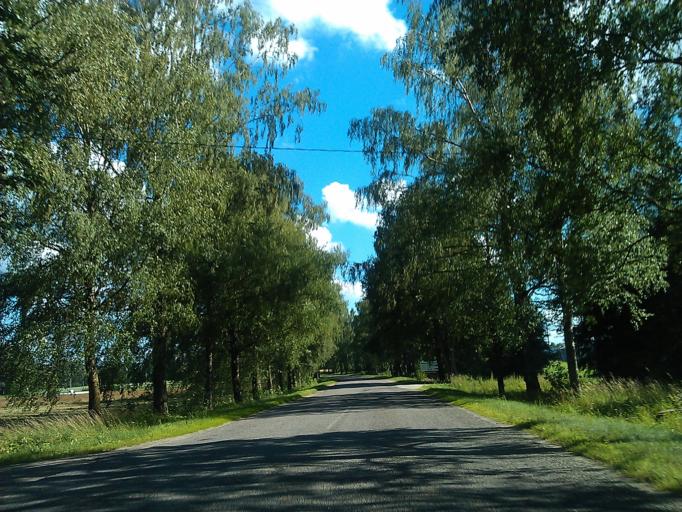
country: LV
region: Rujienas
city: Rujiena
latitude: 57.8682
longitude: 25.3688
